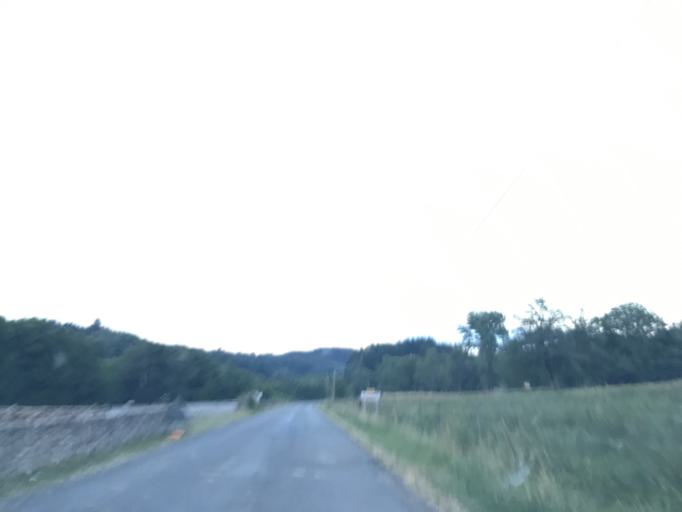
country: FR
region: Auvergne
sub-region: Departement du Puy-de-Dome
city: Chabreloche
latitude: 45.8231
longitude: 3.7053
